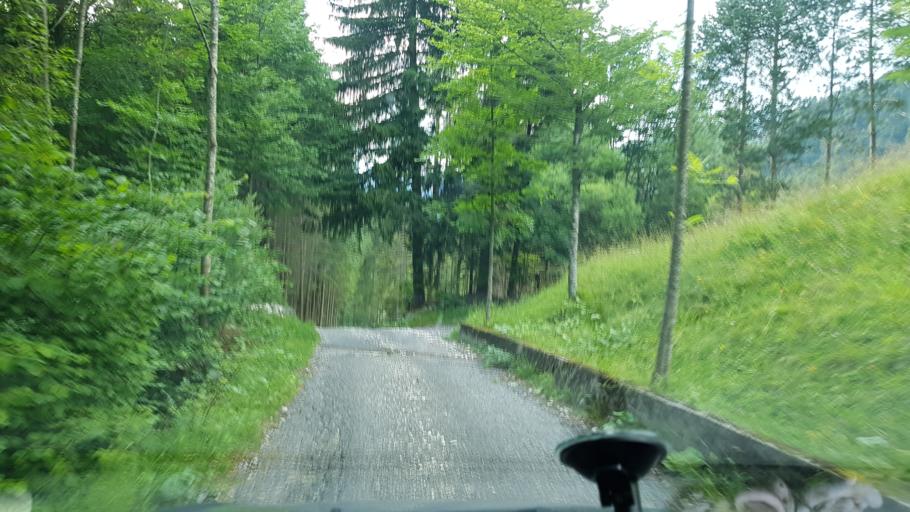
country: IT
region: Friuli Venezia Giulia
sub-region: Provincia di Udine
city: Prato
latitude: 46.3369
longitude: 13.4120
